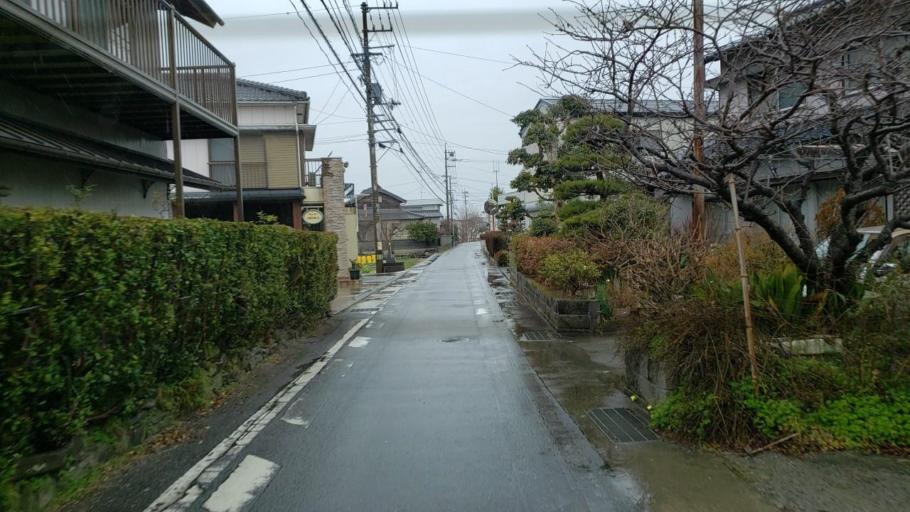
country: JP
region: Tokushima
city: Kamojimacho-jogejima
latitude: 34.0574
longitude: 134.3000
